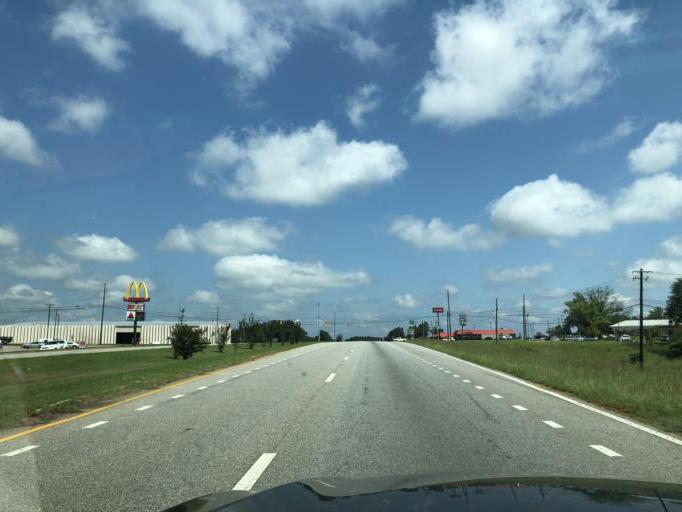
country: US
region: Alabama
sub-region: Henry County
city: Abbeville
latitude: 31.5491
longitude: -85.2852
